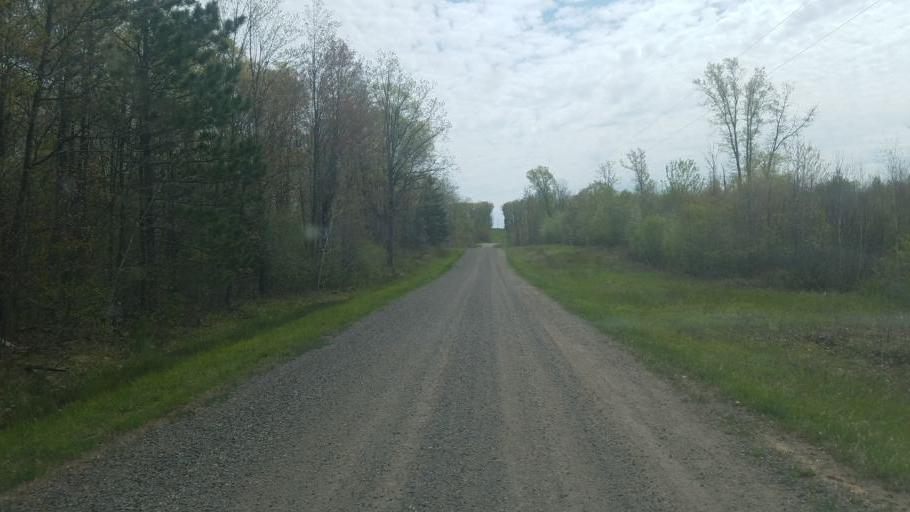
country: US
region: Wisconsin
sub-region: Clark County
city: Neillsville
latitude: 44.4515
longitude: -90.4631
